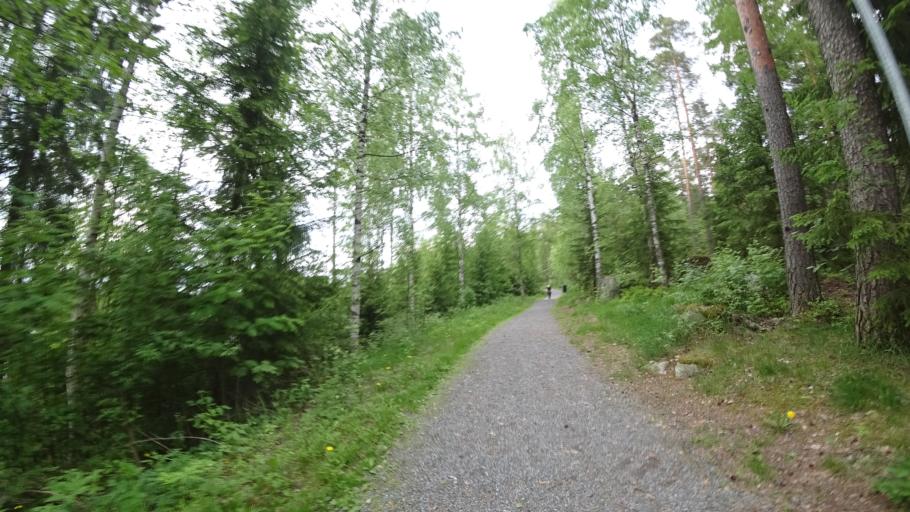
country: FI
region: Pirkanmaa
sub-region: Tampere
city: Yloejaervi
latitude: 61.5208
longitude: 23.6066
